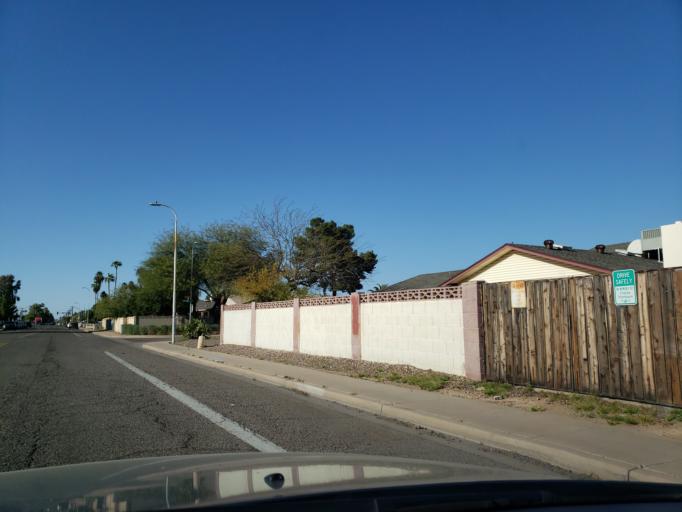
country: US
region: Arizona
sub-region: Maricopa County
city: Glendale
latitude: 33.5213
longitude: -112.1601
